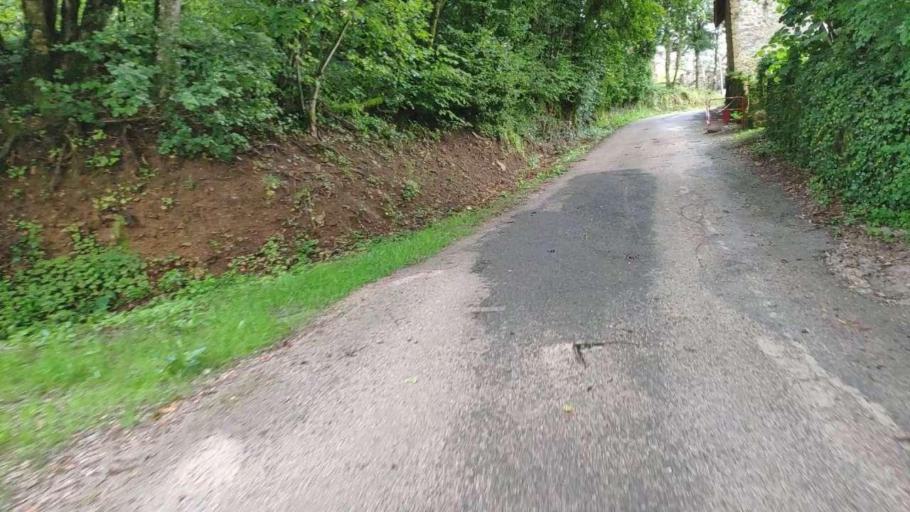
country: FR
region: Franche-Comte
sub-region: Departement du Jura
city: Poligny
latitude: 46.7870
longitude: 5.6193
